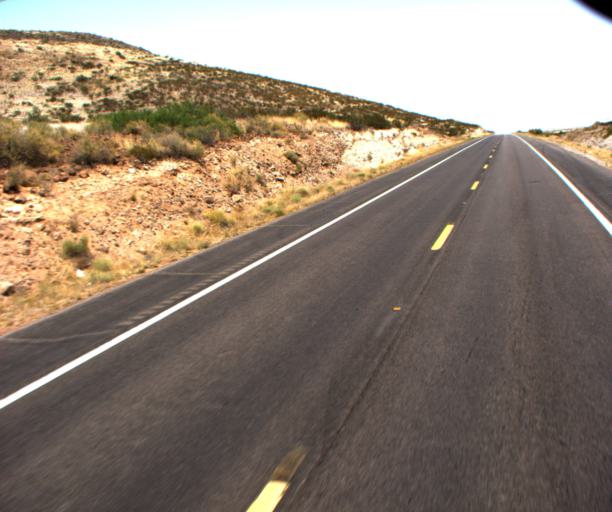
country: US
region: Arizona
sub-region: Greenlee County
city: Clifton
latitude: 32.7345
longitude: -109.1945
